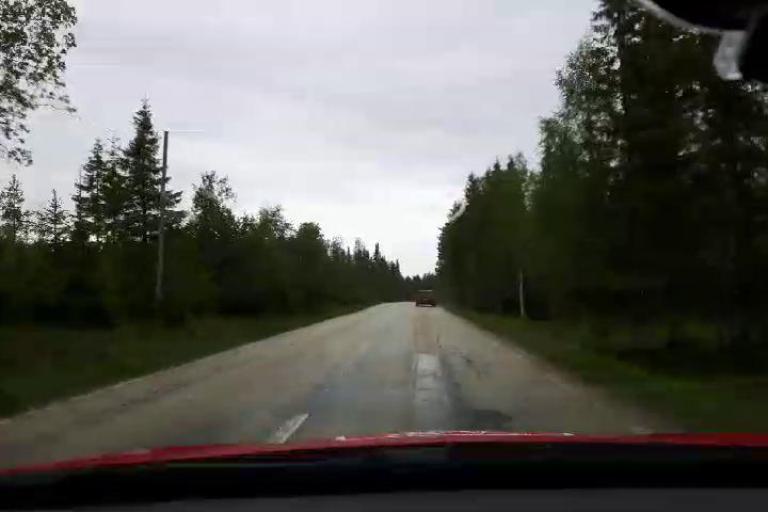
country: SE
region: Jaemtland
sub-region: Bergs Kommun
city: Hoverberg
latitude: 62.8204
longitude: 14.3963
